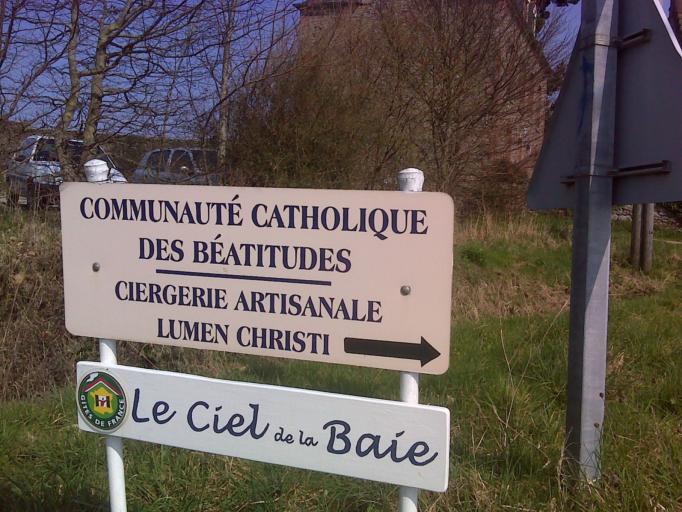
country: FR
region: Brittany
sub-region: Departement d'Ille-et-Vilaine
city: Saint-Broladre
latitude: 48.5844
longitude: -1.6521
